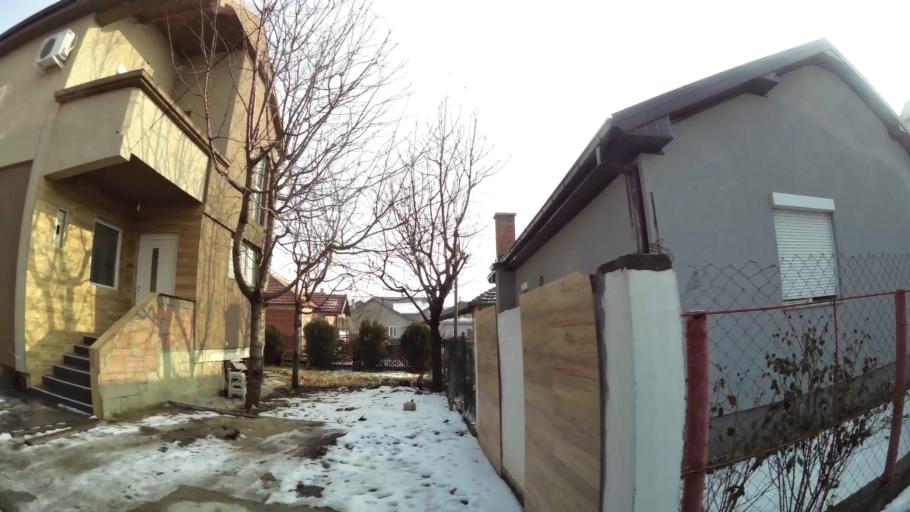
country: MK
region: Ilinden
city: Marino
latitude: 41.9875
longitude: 21.5908
